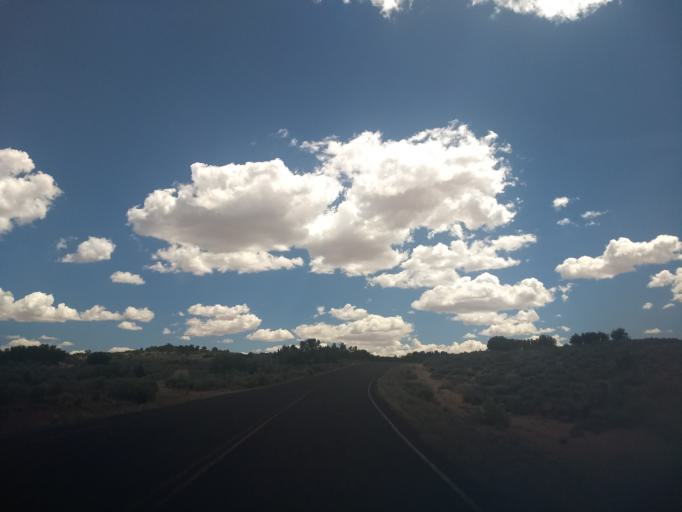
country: US
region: Utah
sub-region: Kane County
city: Kanab
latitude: 37.1306
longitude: -112.6762
